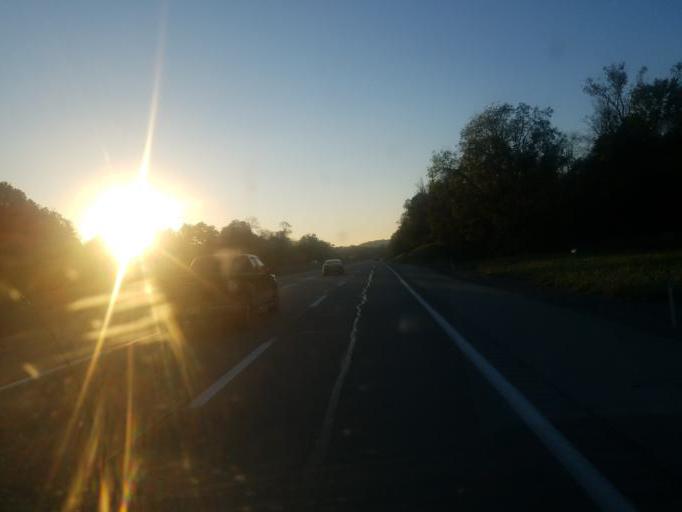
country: US
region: Pennsylvania
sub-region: Lawrence County
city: New Beaver
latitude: 40.8734
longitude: -80.4115
